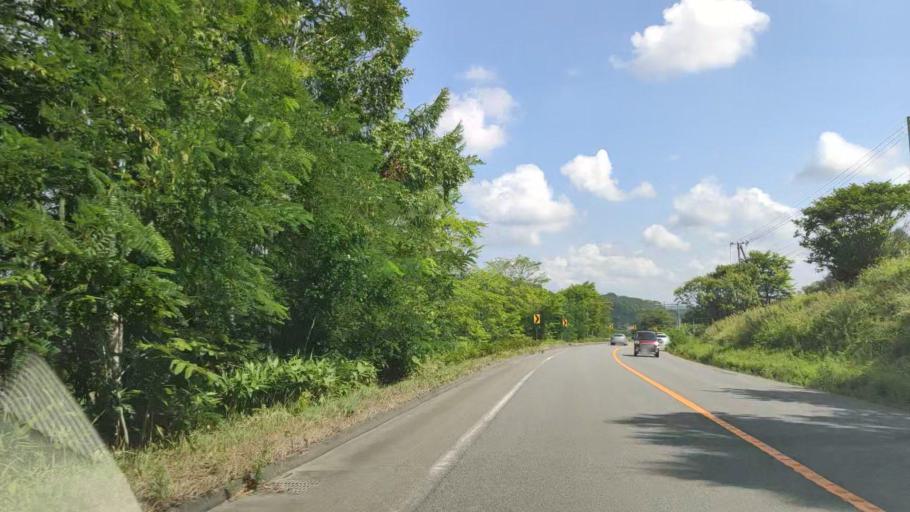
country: JP
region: Hokkaido
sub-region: Asahikawa-shi
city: Asahikawa
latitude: 43.5862
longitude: 142.4445
